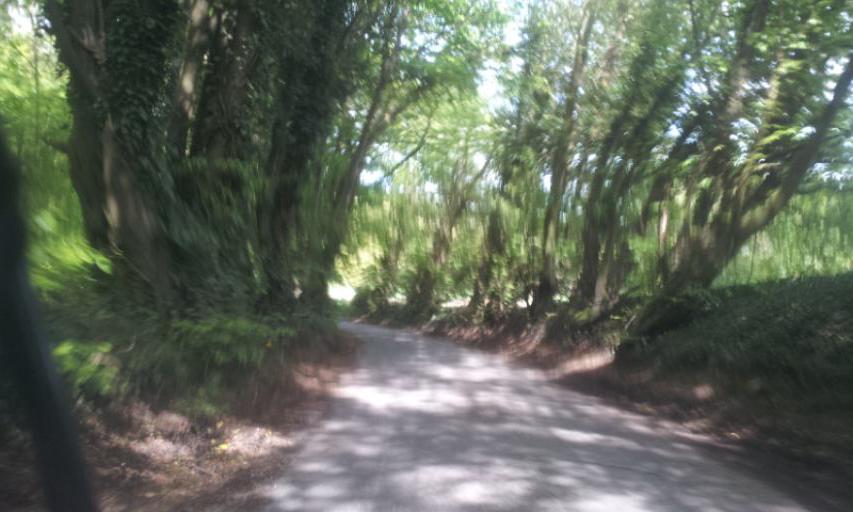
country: GB
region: England
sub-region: Medway
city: Halling
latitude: 51.3785
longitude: 0.4129
